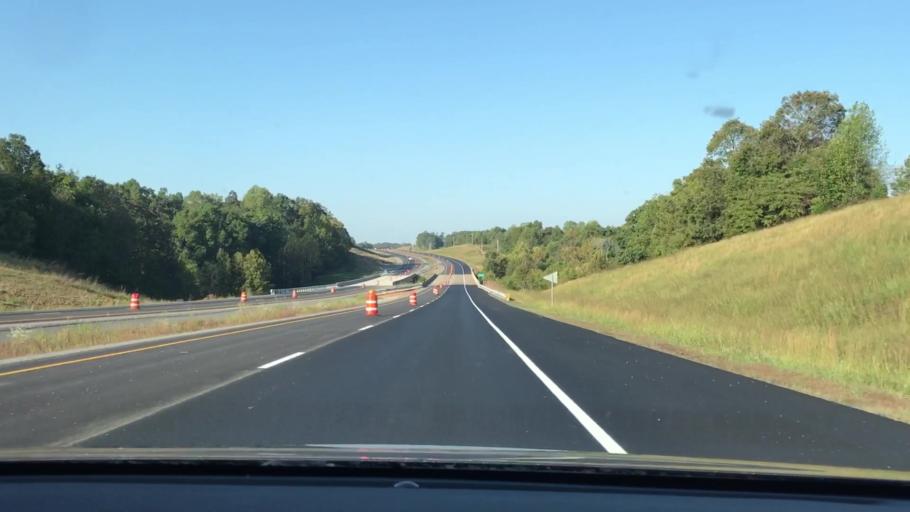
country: US
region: Kentucky
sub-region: Trigg County
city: Cadiz
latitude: 36.8425
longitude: -87.8299
